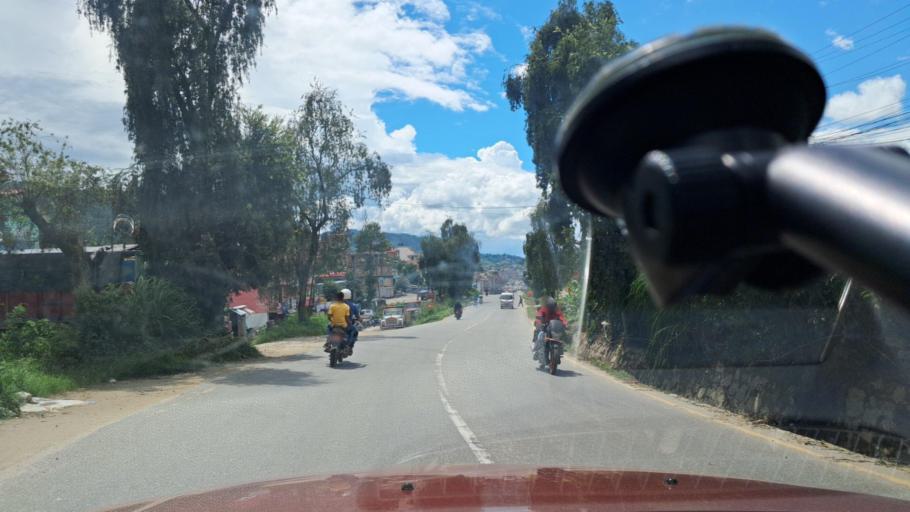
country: NP
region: Central Region
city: Banepa
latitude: 27.6278
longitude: 85.5346
